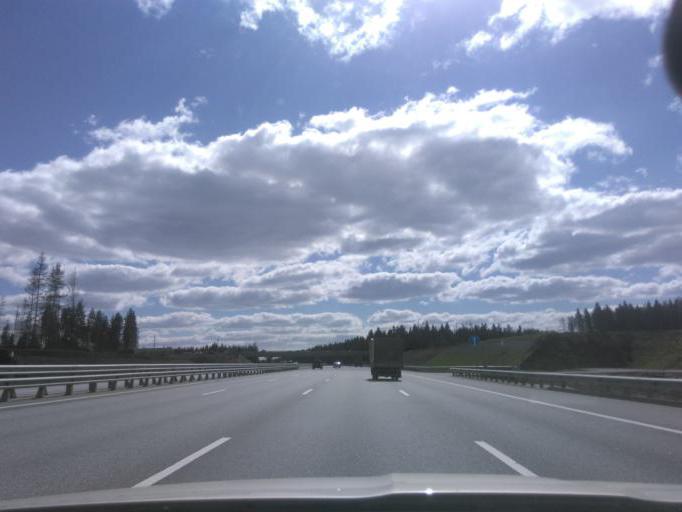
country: RU
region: Moskovskaya
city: Skhodnya
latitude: 55.9739
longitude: 37.3247
